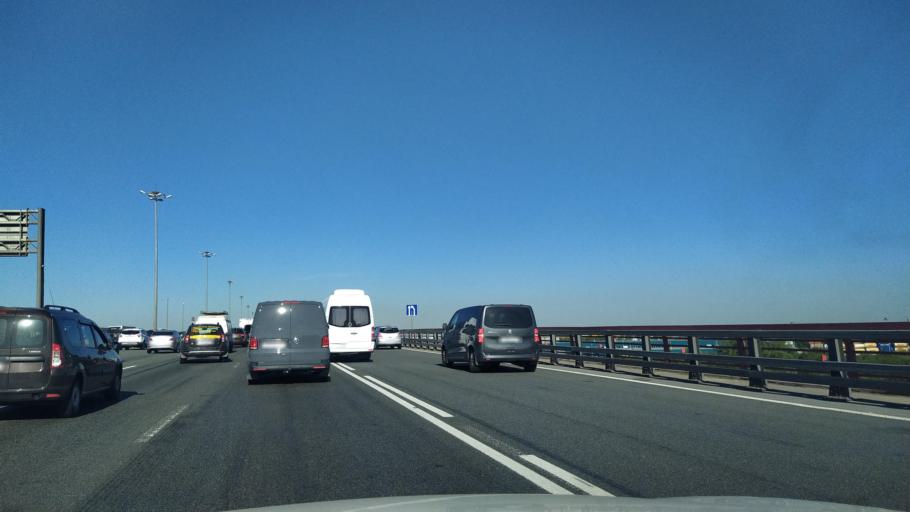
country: RU
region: St.-Petersburg
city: Shushary
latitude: 59.8162
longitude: 30.3867
